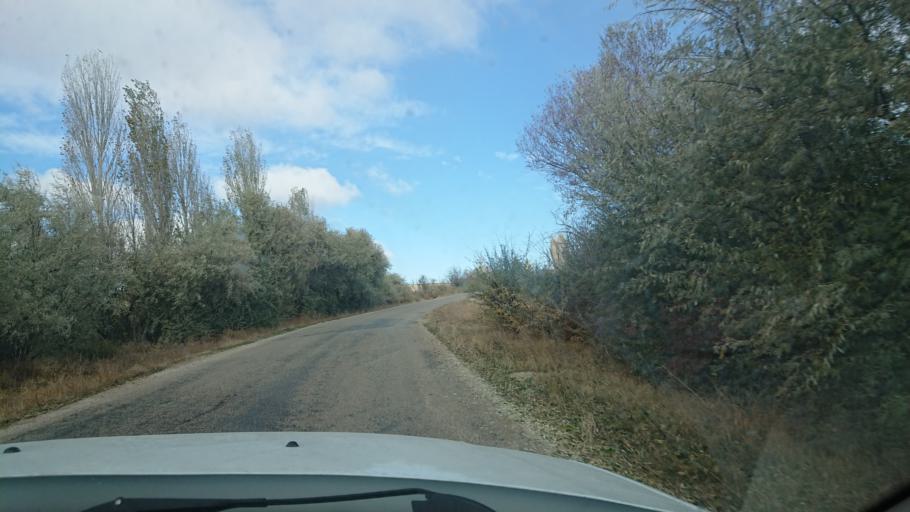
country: TR
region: Aksaray
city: Agacoren
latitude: 38.8301
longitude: 33.9563
